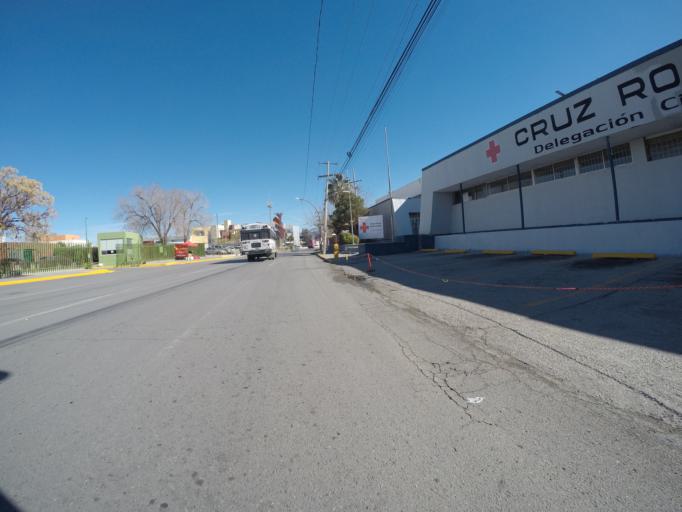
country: MX
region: Chihuahua
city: Ciudad Juarez
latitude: 31.7413
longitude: -106.4475
